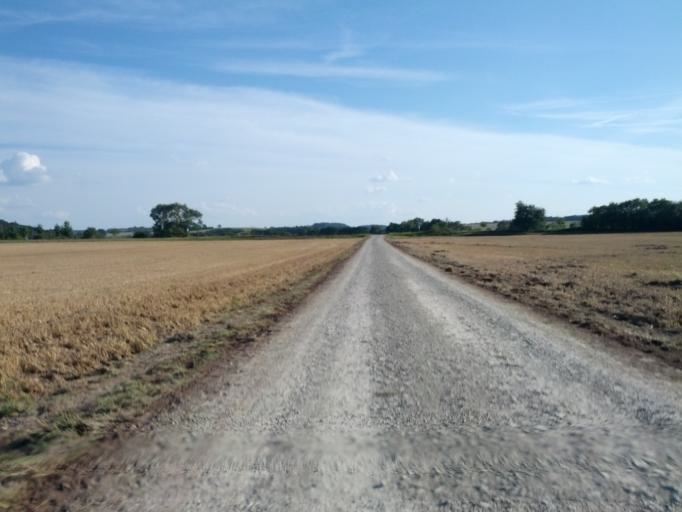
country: DE
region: Thuringia
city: Creuzburg
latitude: 51.0459
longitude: 10.2498
